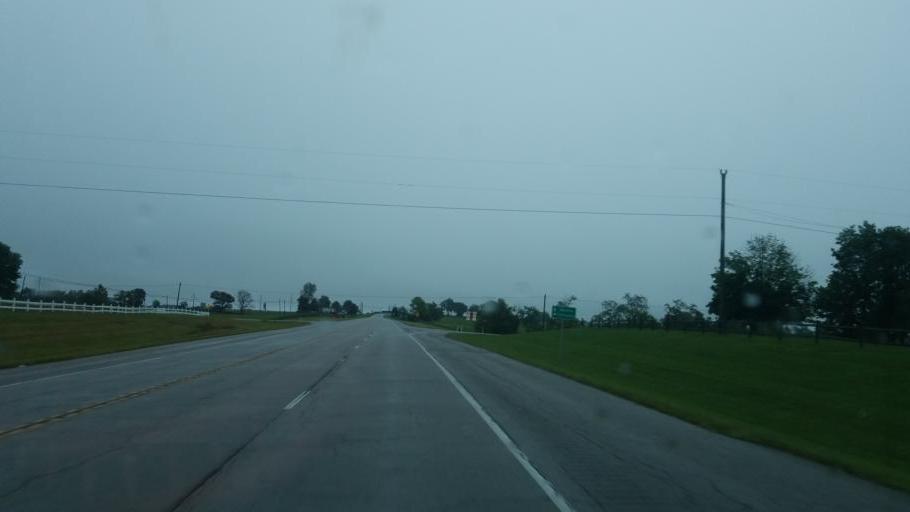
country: US
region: Kentucky
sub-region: Fleming County
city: Flemingsburg
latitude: 38.3957
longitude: -83.7072
